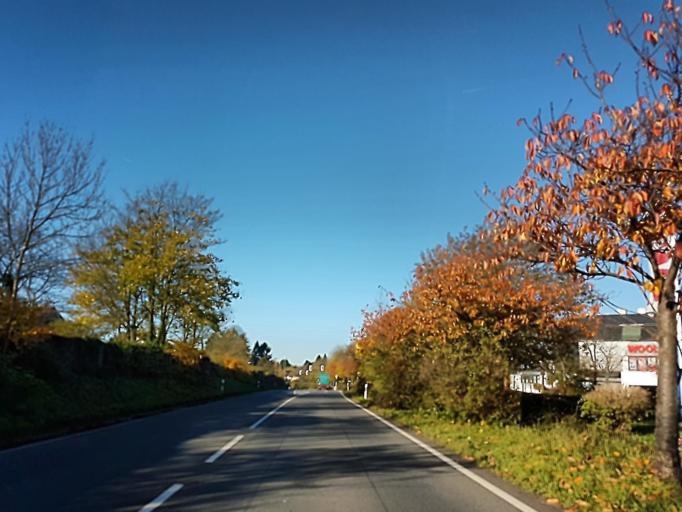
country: DE
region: North Rhine-Westphalia
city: Radevormwald
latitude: 51.2009
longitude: 7.3617
